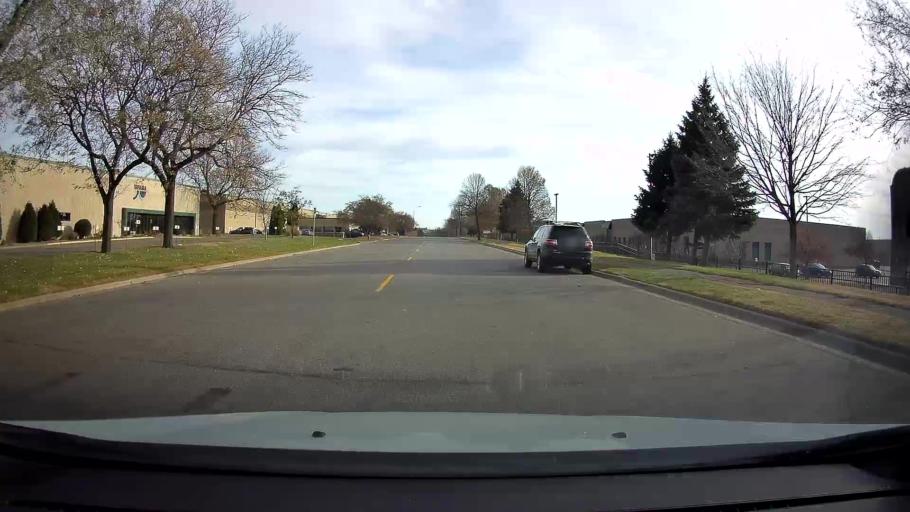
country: US
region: Minnesota
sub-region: Ramsey County
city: Lauderdale
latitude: 44.9828
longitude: -93.2158
